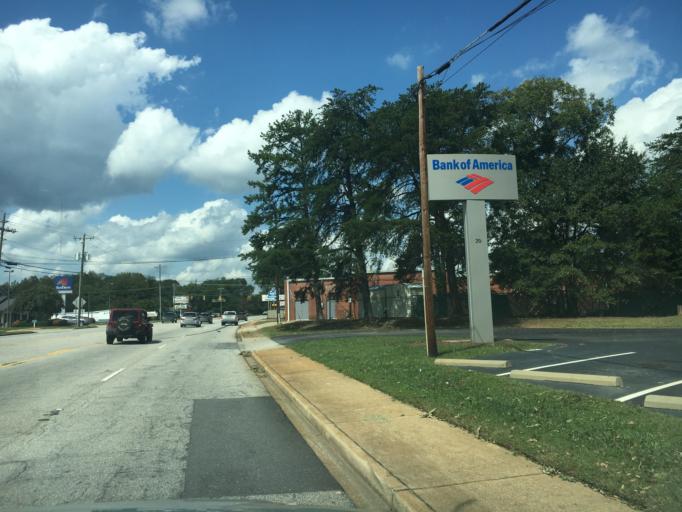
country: US
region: South Carolina
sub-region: Greenville County
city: Berea
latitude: 34.8837
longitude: -82.4567
